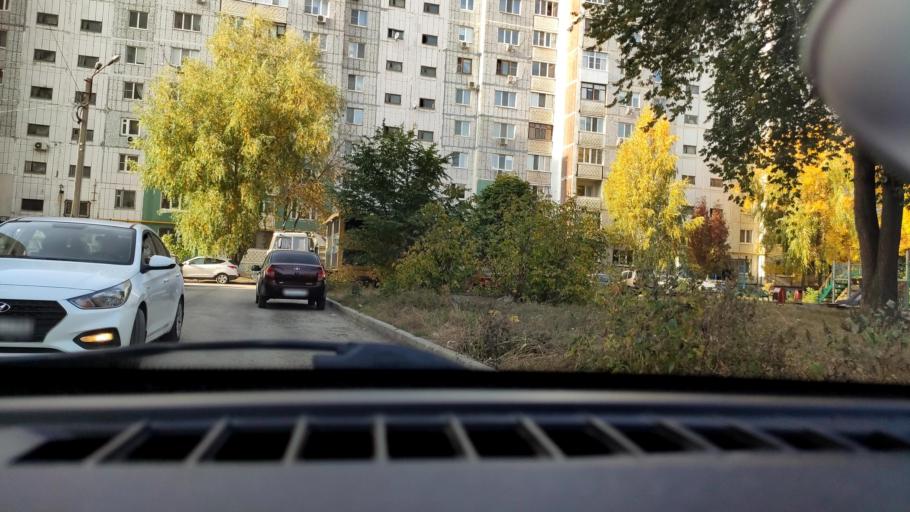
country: RU
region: Samara
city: Samara
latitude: 53.1883
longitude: 50.2142
